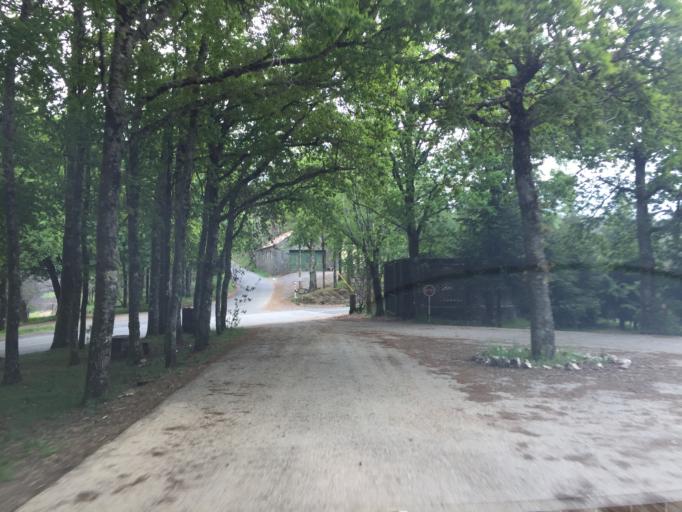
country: PT
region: Coimbra
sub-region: Arganil
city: Arganil
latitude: 40.1853
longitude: -7.9760
